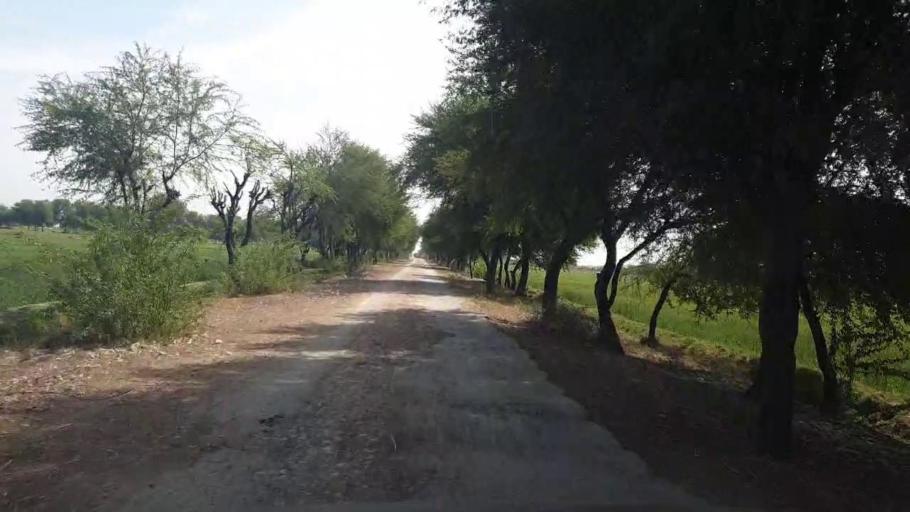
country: PK
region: Sindh
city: Umarkot
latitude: 25.3320
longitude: 69.6120
